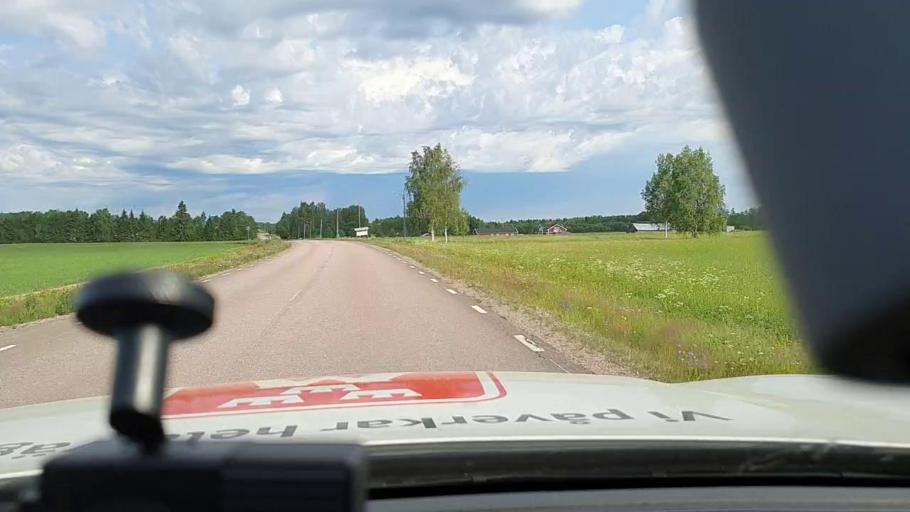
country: SE
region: Norrbotten
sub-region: Bodens Kommun
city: Saevast
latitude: 65.6939
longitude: 21.7811
